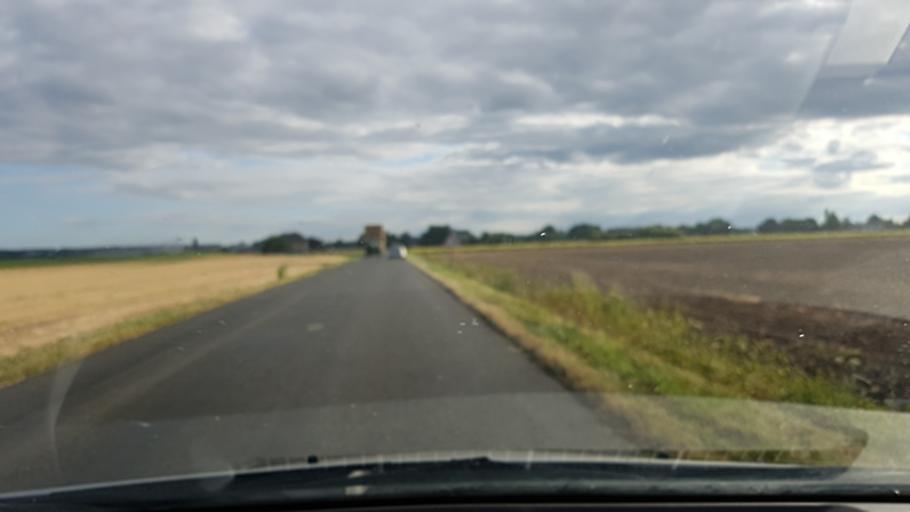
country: FR
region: Pays de la Loire
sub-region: Departement de Maine-et-Loire
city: Saint-Mathurin-sur-Loire
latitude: 47.4350
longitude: -0.2953
